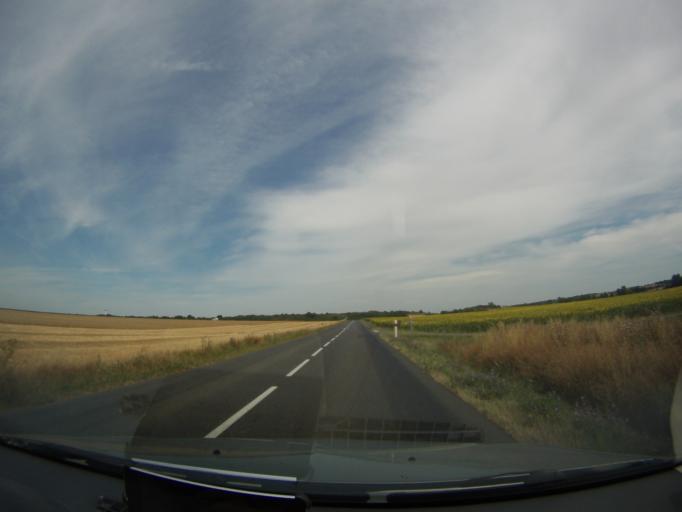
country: FR
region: Poitou-Charentes
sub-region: Departement de la Vienne
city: Saint-Jean-de-Sauves
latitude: 46.8051
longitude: 0.0457
